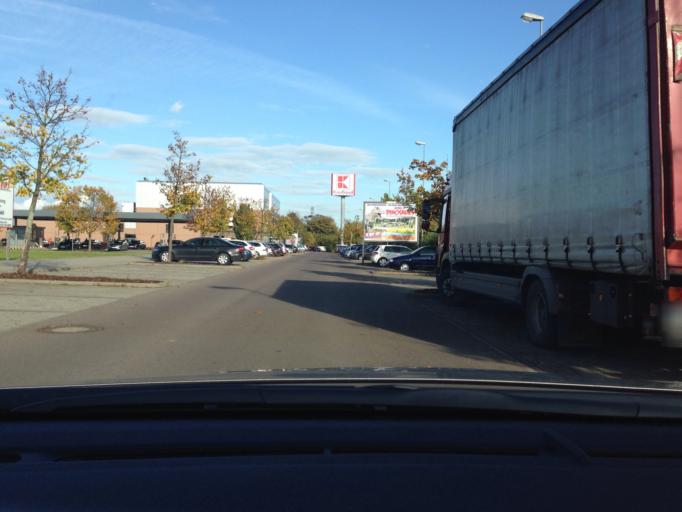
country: DE
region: Saxony
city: Taucha
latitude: 51.3664
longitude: 12.4568
